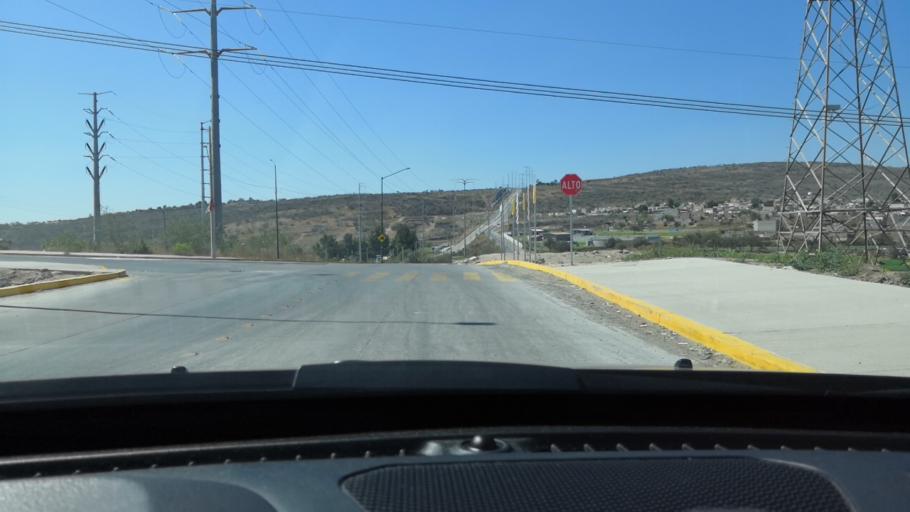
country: MX
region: Guanajuato
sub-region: Leon
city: Centro Familiar la Soledad
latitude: 21.1269
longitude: -101.7354
